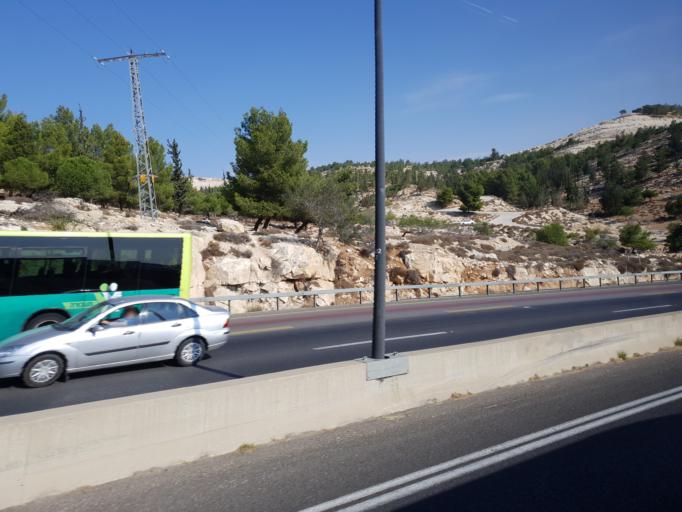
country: PS
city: Az Za`ayyim
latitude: 31.7885
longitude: 35.2760
